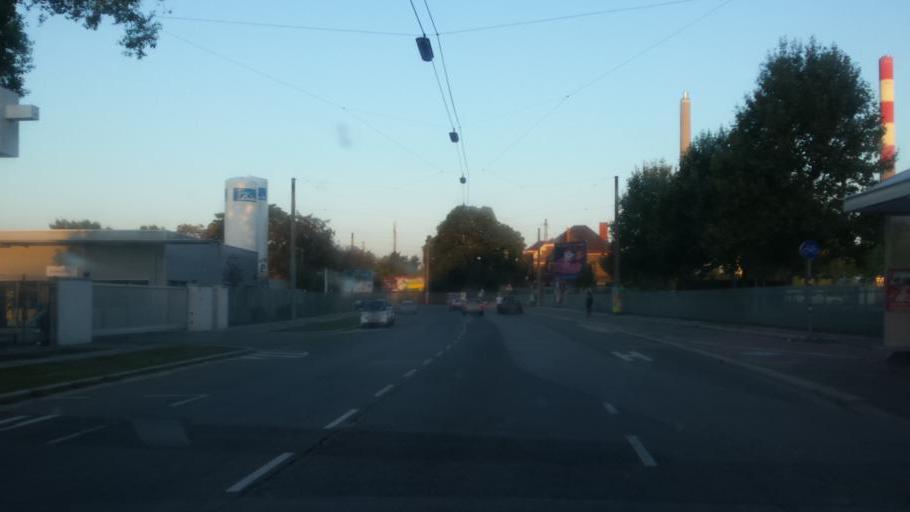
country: AT
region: Vienna
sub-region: Wien Stadt
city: Vienna
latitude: 48.1854
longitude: 16.4269
